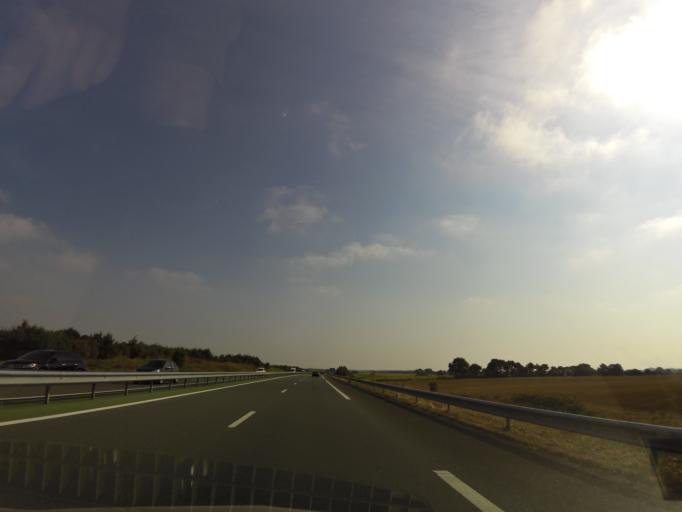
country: FR
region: Pays de la Loire
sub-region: Departement de la Vendee
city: Les Essarts
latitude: 46.7846
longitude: -1.2515
